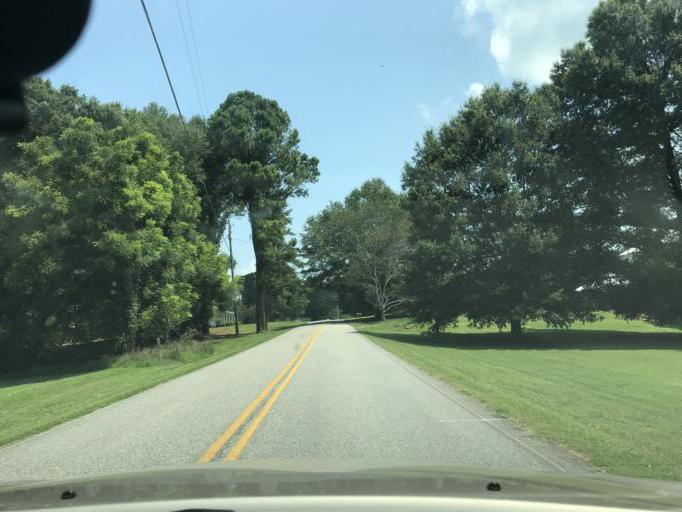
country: US
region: Georgia
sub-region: Dawson County
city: Dawsonville
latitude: 34.3252
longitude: -84.0900
